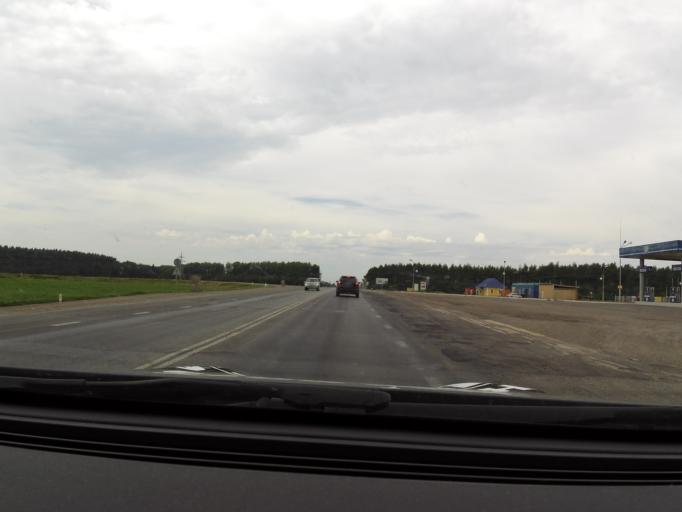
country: RU
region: Bashkortostan
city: Iglino
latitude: 54.7460
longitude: 56.3159
